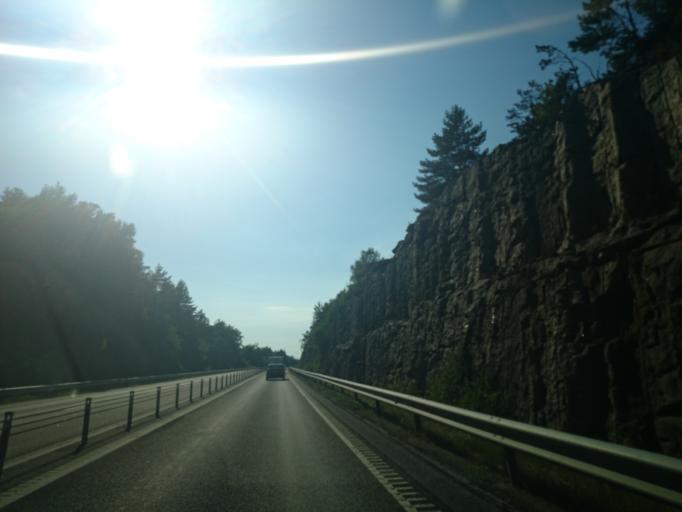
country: SE
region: Blekinge
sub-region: Ronneby Kommun
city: Brakne-Hoby
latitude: 56.2176
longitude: 15.1870
